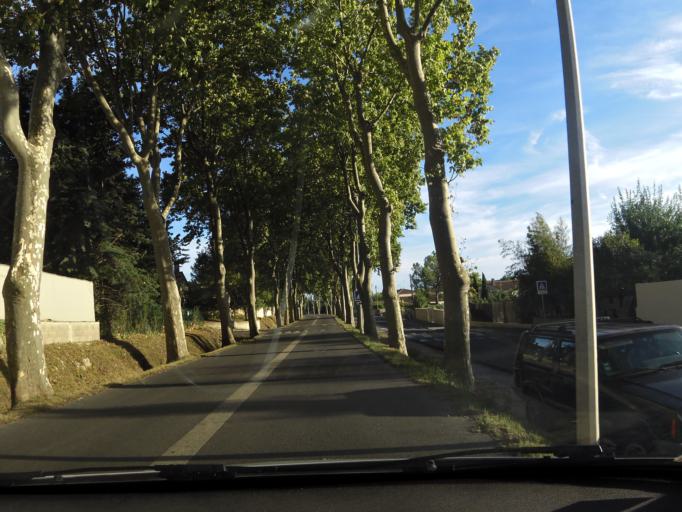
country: FR
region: Languedoc-Roussillon
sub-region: Departement de l'Herault
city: Prades-le-Lez
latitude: 43.6910
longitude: 3.8627
